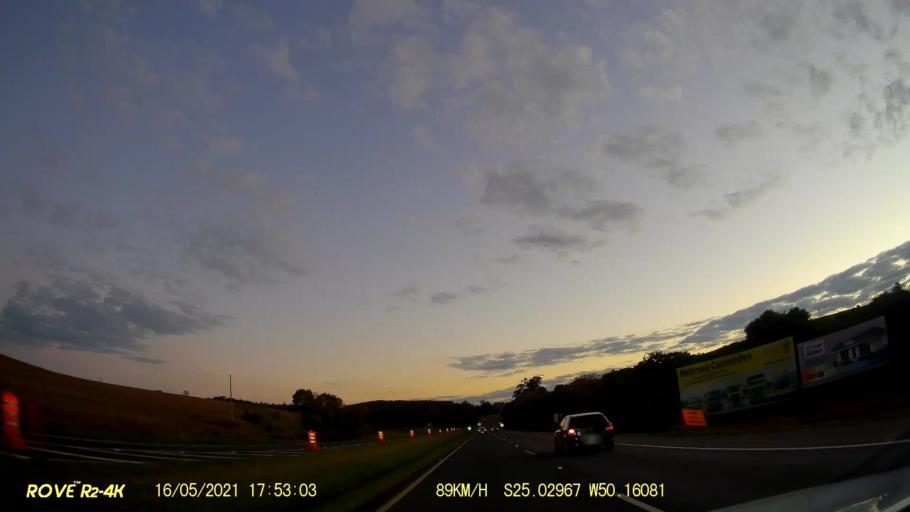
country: BR
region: Parana
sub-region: Ponta Grossa
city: Ponta Grossa
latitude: -25.0298
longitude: -50.1608
